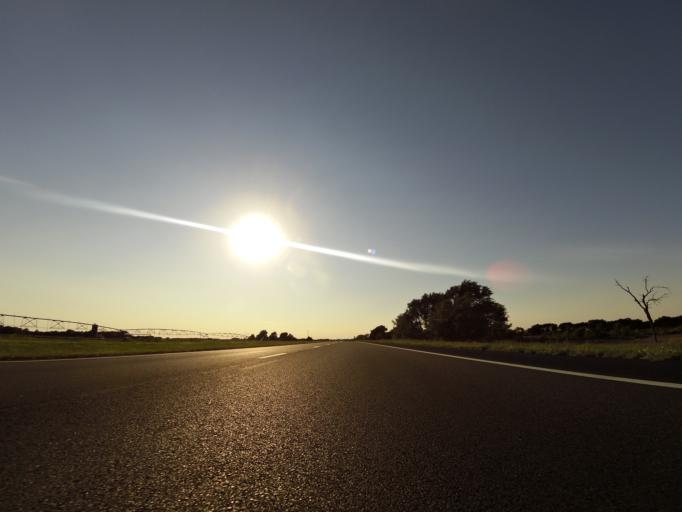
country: US
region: Kansas
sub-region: Reno County
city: Haven
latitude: 37.8885
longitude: -97.7444
